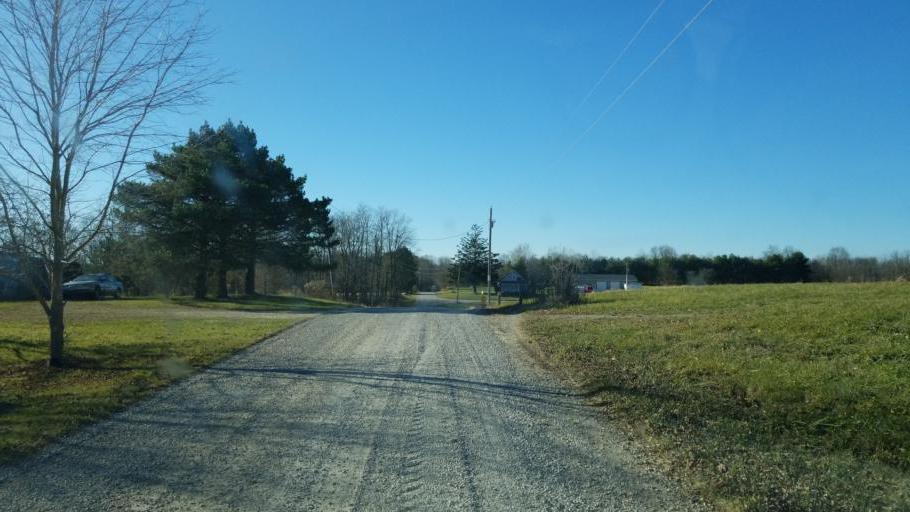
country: US
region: Ohio
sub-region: Morrow County
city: Mount Gilead
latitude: 40.5359
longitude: -82.6993
